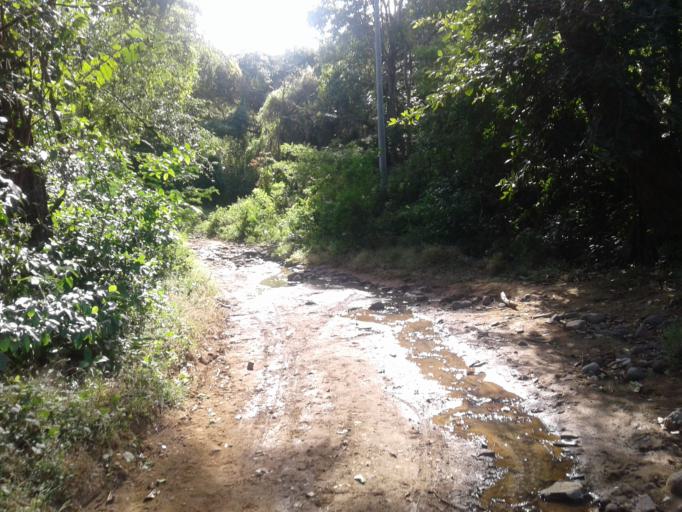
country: NI
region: Carazo
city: Santa Teresa
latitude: 11.6303
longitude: -86.1940
